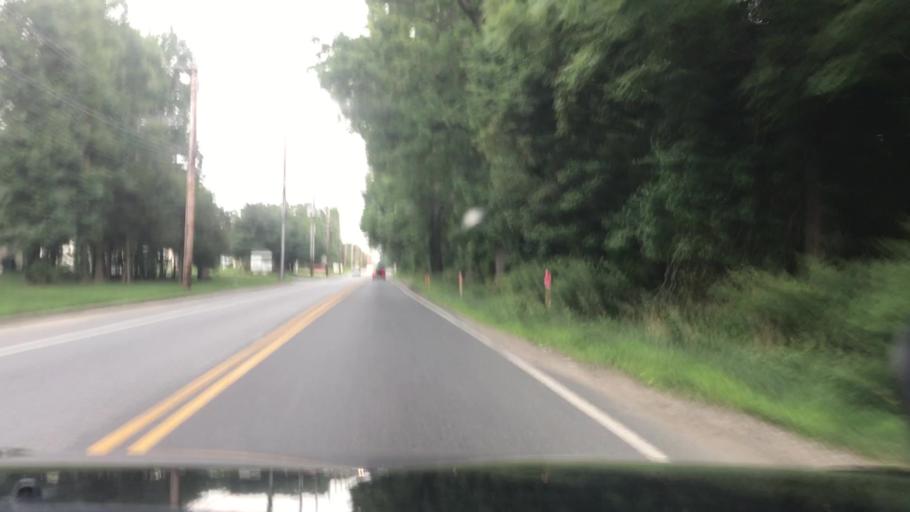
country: US
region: New Jersey
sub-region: Ocean County
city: Lakewood
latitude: 40.0716
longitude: -74.2456
